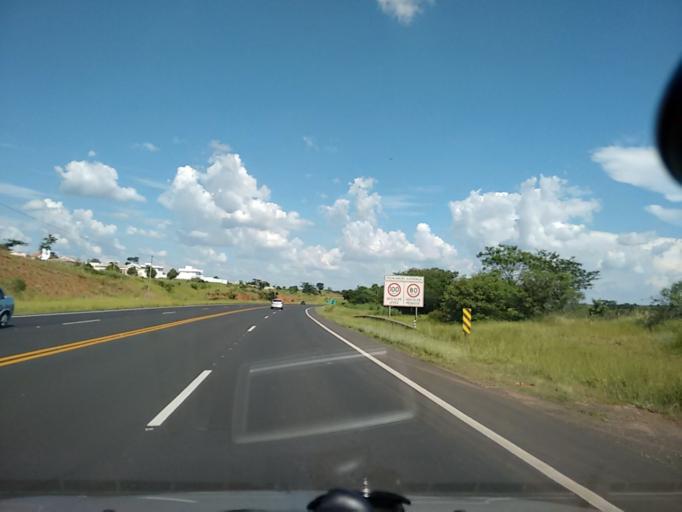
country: BR
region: Sao Paulo
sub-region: Pompeia
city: Pompeia
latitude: -22.1190
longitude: -50.1522
